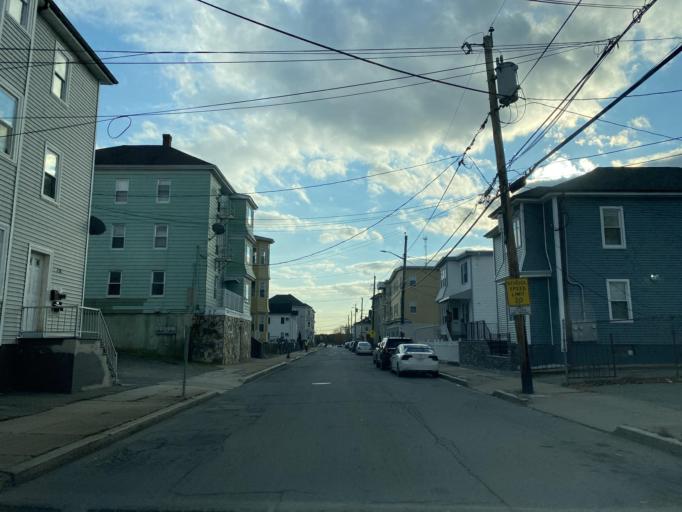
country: US
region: Massachusetts
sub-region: Bristol County
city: Fall River
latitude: 41.6915
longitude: -71.1377
